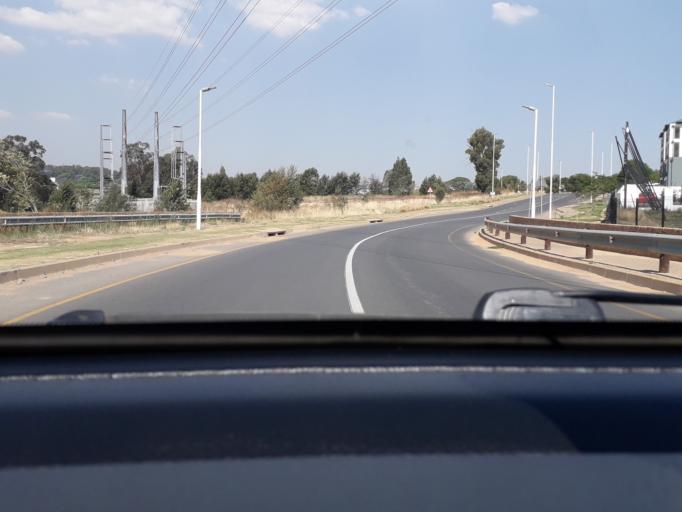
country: ZA
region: Gauteng
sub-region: City of Johannesburg Metropolitan Municipality
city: Modderfontein
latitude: -26.0942
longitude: 28.1446
